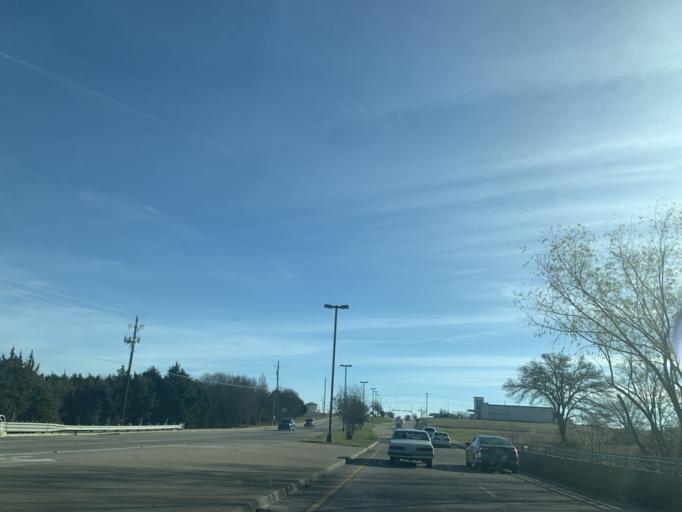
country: US
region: Texas
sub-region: Dallas County
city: Shamrock
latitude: 32.5897
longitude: -96.8778
